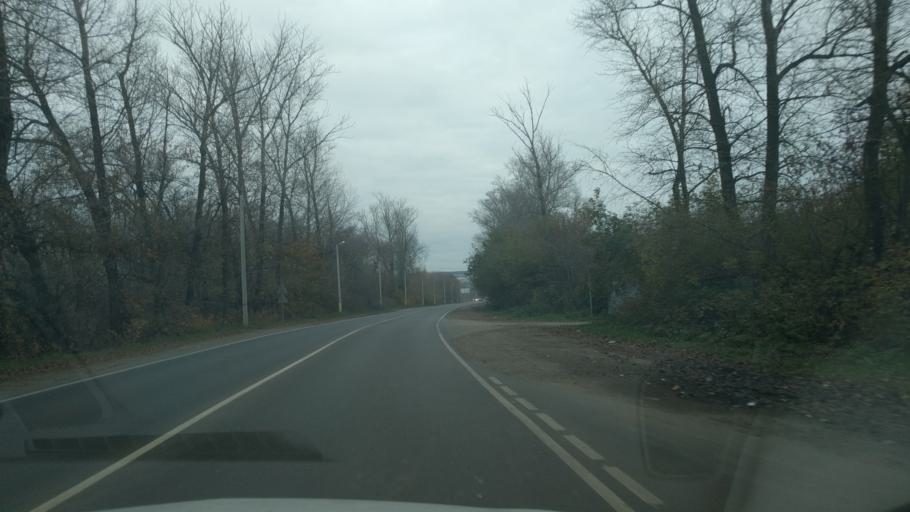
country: RU
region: Moskovskaya
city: Lopatinskiy
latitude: 55.3303
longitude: 38.7136
